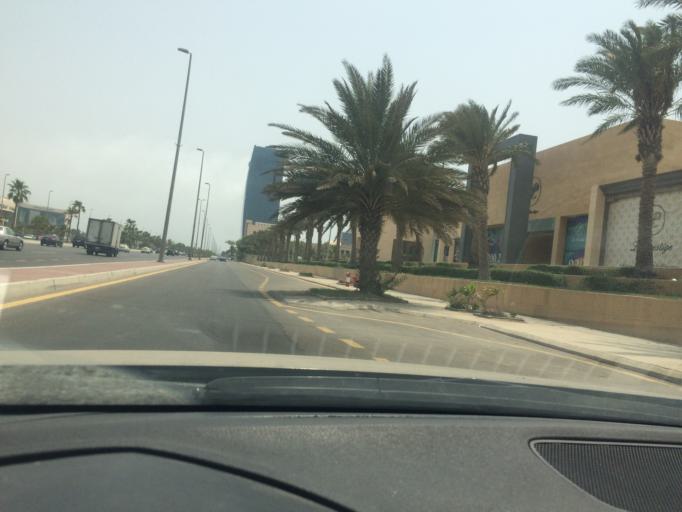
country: SA
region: Makkah
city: Jeddah
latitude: 21.5659
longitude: 39.1258
